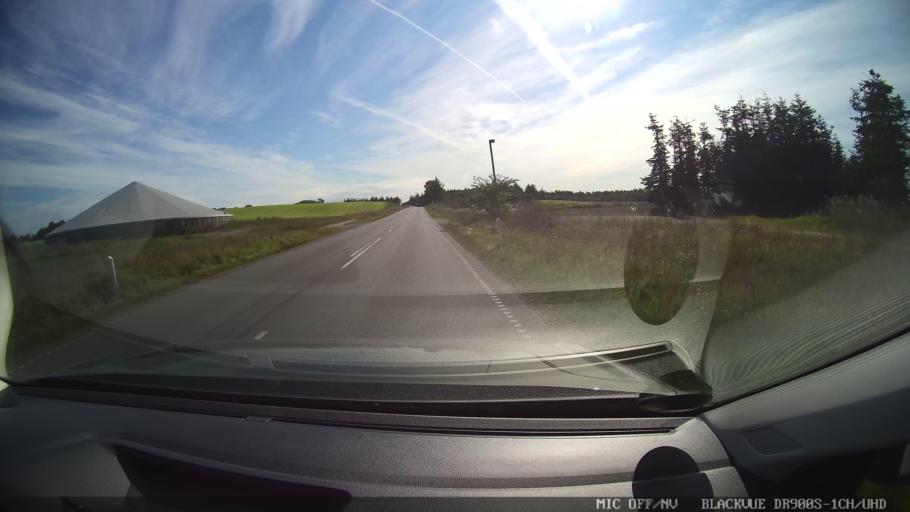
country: DK
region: North Denmark
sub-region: Mariagerfjord Kommune
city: Arden
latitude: 56.7626
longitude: 9.9132
